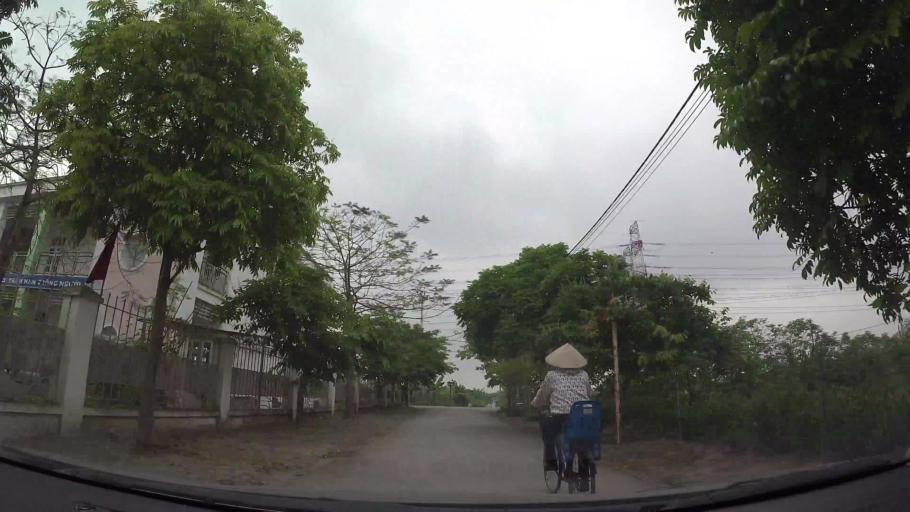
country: VN
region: Ha Noi
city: Trau Quy
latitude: 21.0691
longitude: 105.9203
